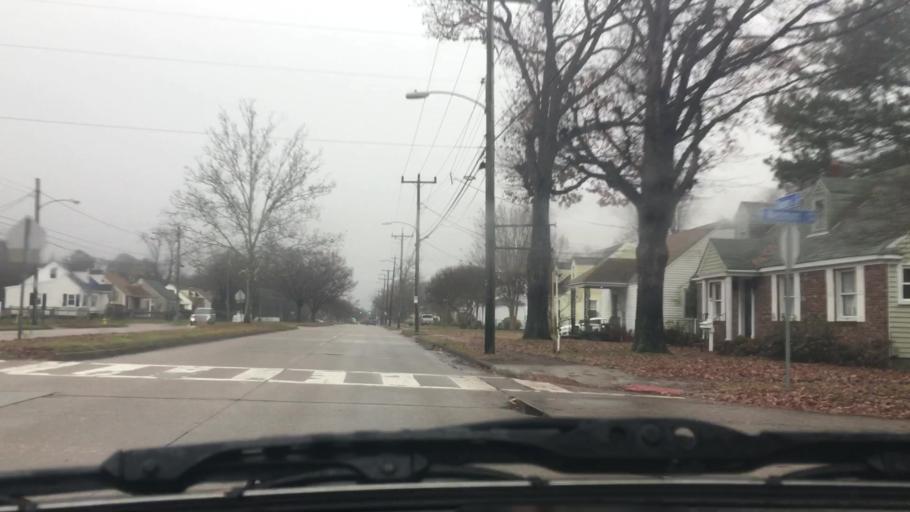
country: US
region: Virginia
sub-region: City of Norfolk
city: Norfolk
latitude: 36.9364
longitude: -76.2543
